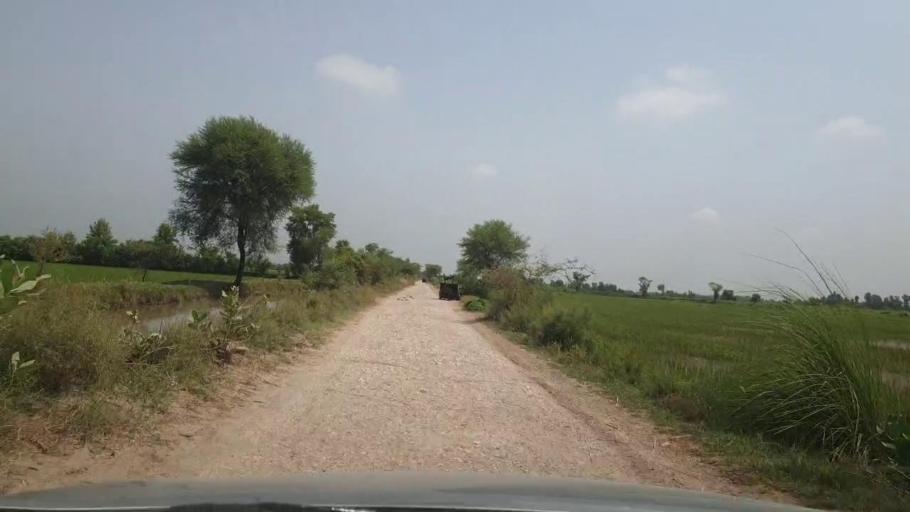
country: PK
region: Sindh
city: Garhi Yasin
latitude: 27.9393
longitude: 68.3696
